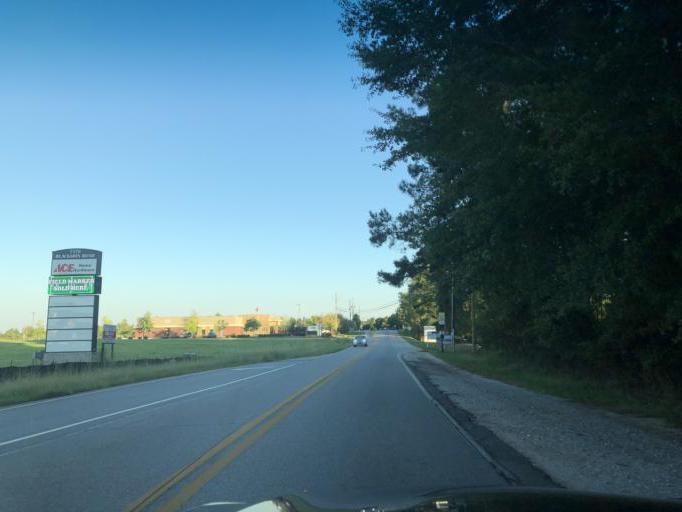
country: US
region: Georgia
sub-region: Muscogee County
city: Columbus
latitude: 32.5511
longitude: -84.8964
